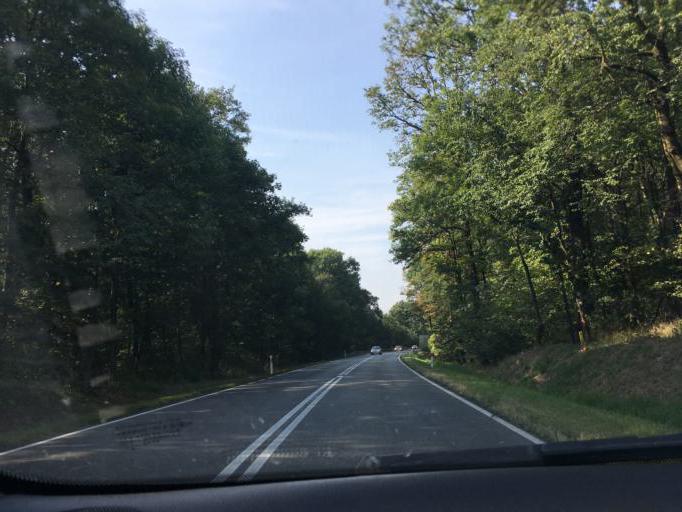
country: PL
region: Opole Voivodeship
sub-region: Powiat nyski
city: Nysa
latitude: 50.4338
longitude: 17.4106
